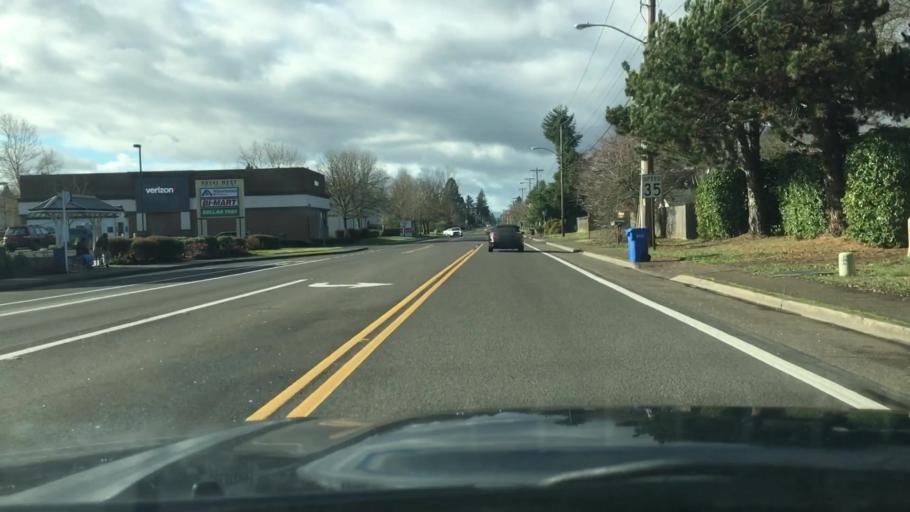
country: US
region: Oregon
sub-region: Lane County
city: Eugene
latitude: 44.0701
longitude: -123.1788
